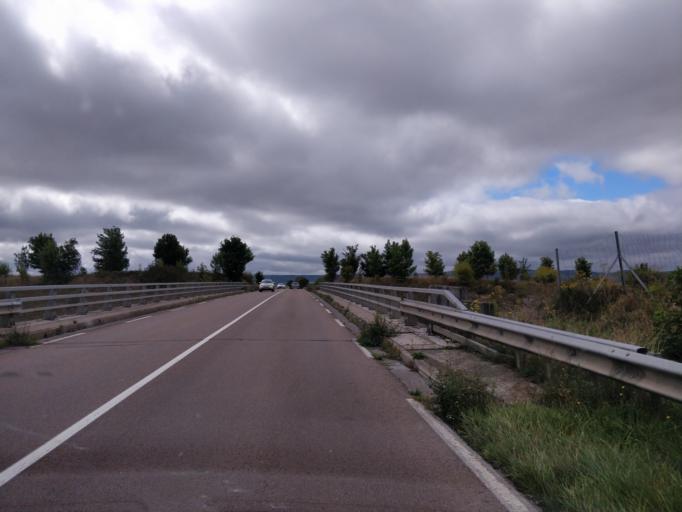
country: FR
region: Champagne-Ardenne
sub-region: Departement de l'Aube
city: Saint-Pouange
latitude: 48.2365
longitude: 4.0197
